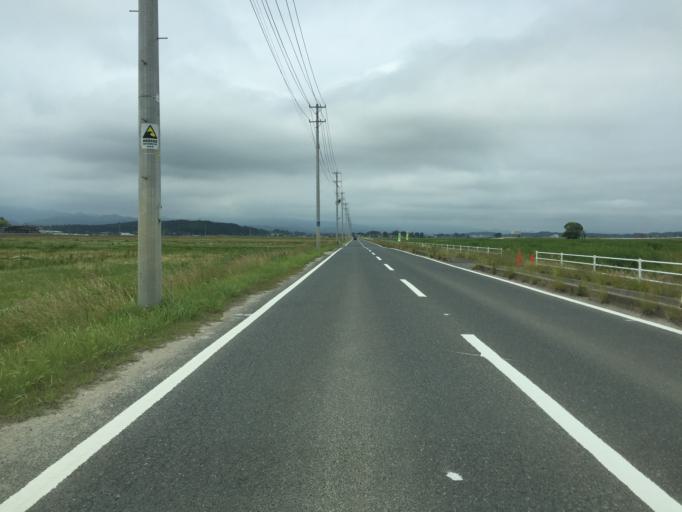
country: JP
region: Fukushima
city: Namie
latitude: 37.6811
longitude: 140.9984
